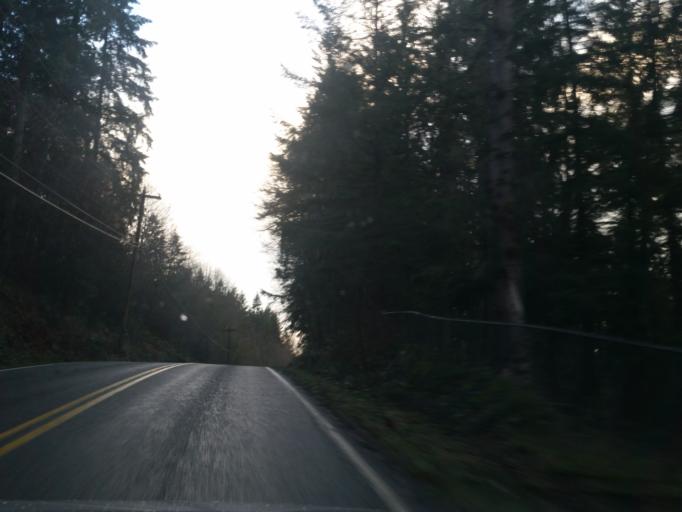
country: US
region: Washington
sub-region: Snohomish County
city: Cathcart
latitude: 47.8277
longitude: -122.0935
